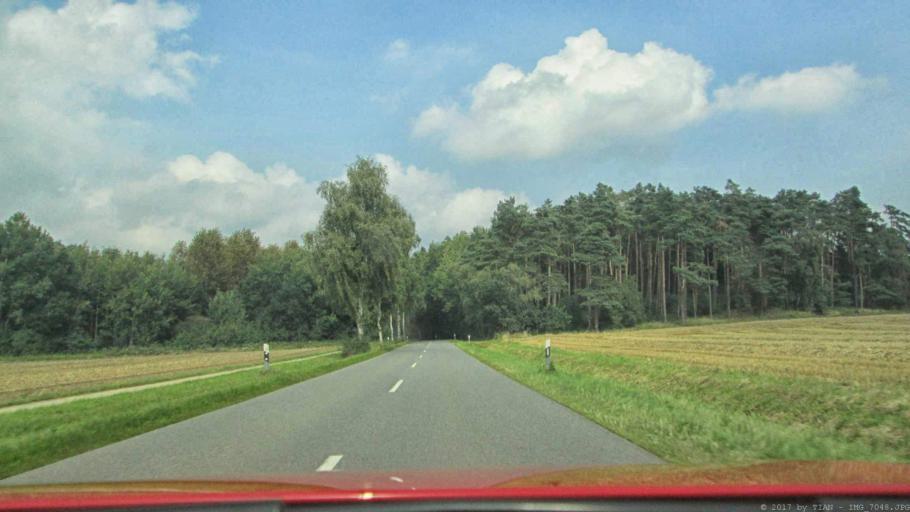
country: DE
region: Lower Saxony
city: Thomasburg
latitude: 53.2055
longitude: 10.6446
